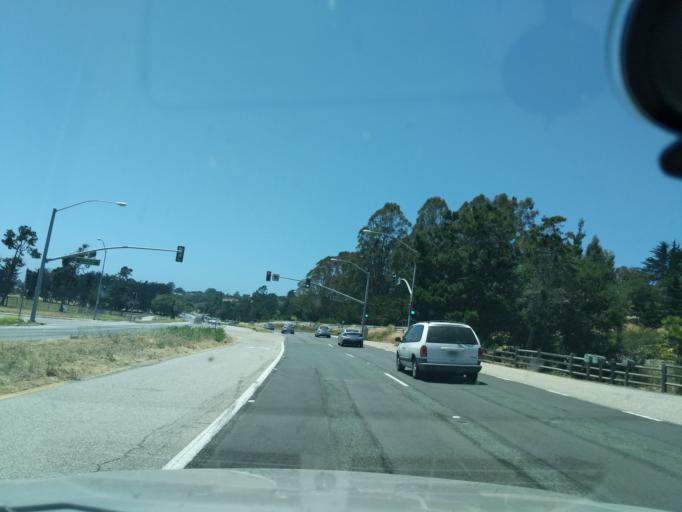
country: US
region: California
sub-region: Monterey County
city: Carmel-by-the-Sea
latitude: 36.5439
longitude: -121.8962
